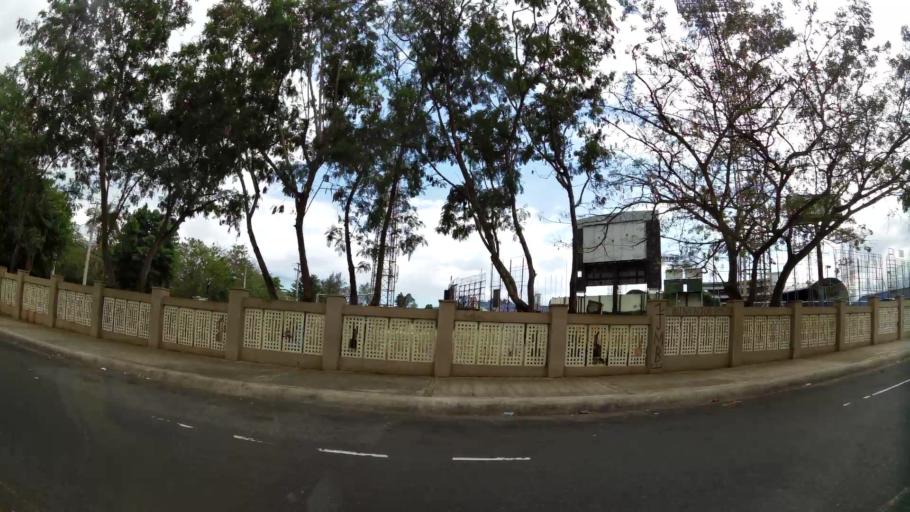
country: DO
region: Nacional
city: La Agustina
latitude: 18.4897
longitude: -69.9255
